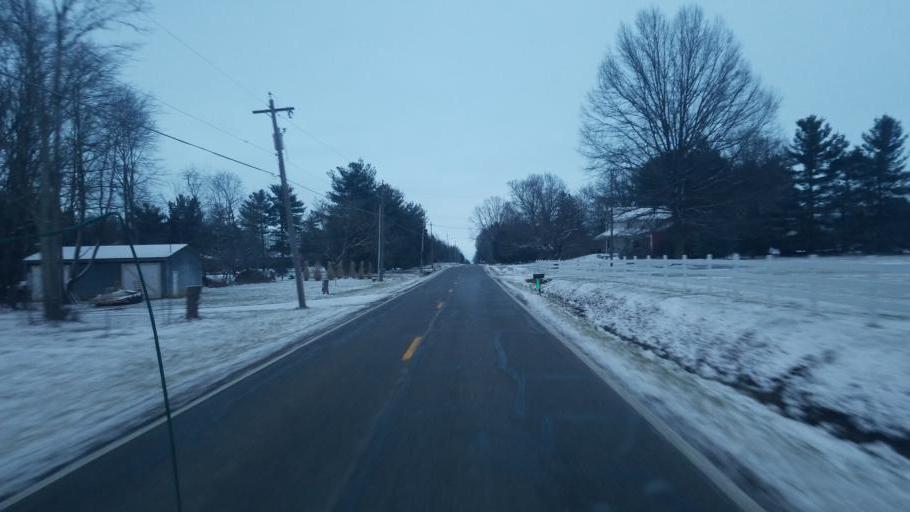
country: US
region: Ohio
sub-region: Delaware County
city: Sunbury
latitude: 40.1881
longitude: -82.8493
